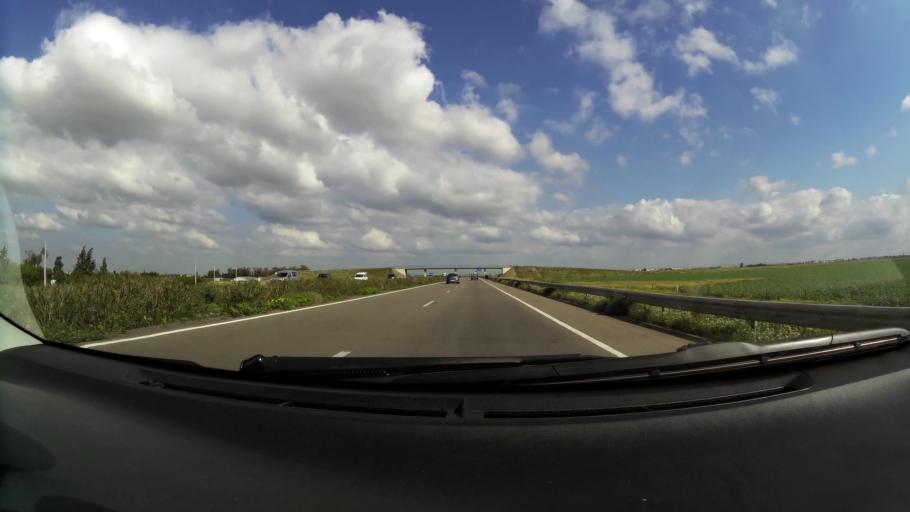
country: MA
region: Chaouia-Ouardigha
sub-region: Settat Province
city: Berrechid
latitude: 33.3078
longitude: -7.5871
